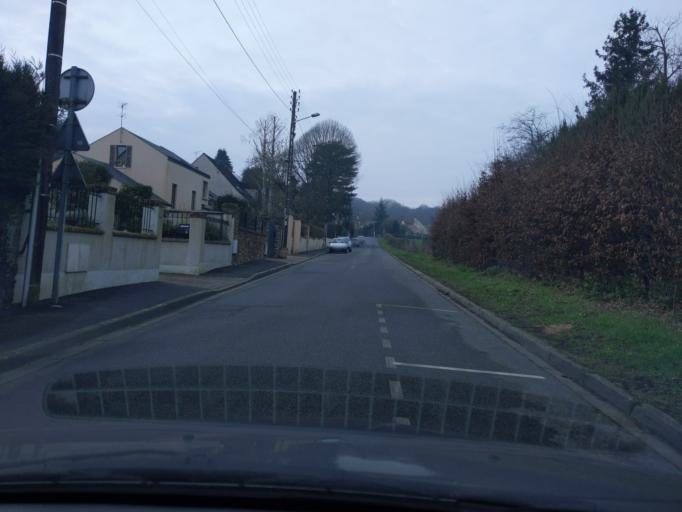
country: FR
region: Ile-de-France
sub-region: Departement des Yvelines
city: Saint-Remy-les-Chevreuse
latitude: 48.7166
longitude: 2.0648
